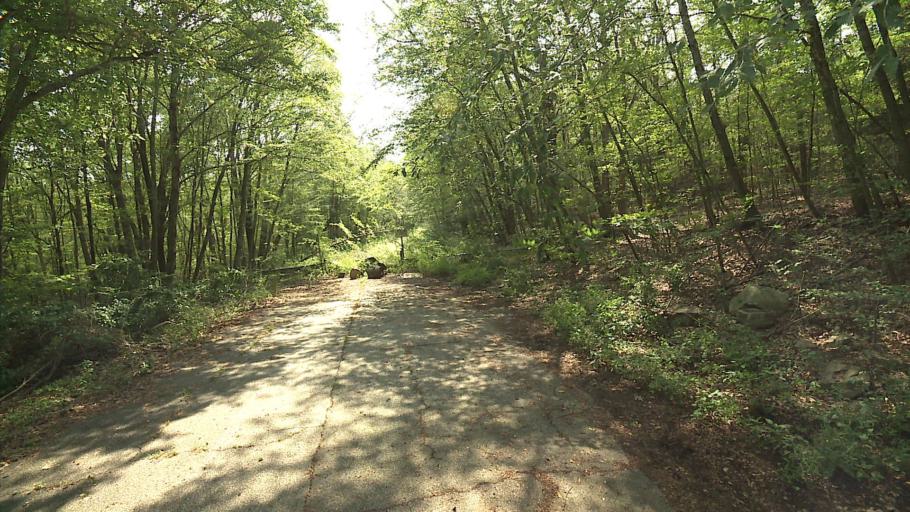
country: US
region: Connecticut
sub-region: New London County
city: Montville Center
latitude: 41.5739
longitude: -72.2038
